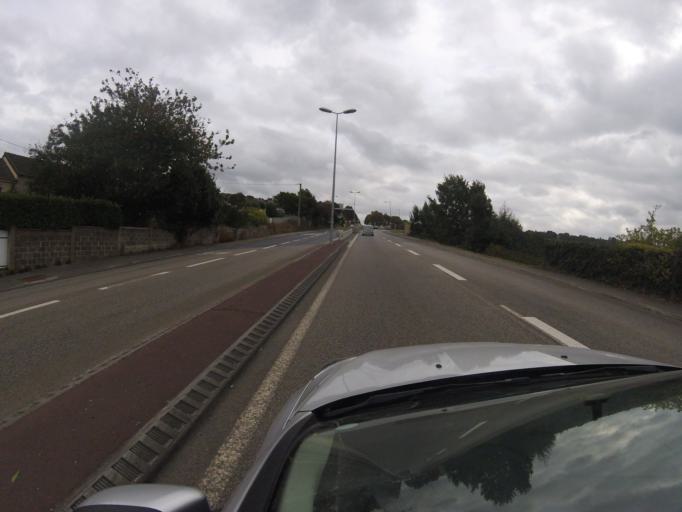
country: FR
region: Lower Normandy
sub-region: Departement de la Manche
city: Cherbourg-Octeville
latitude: 49.6205
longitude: -1.6143
